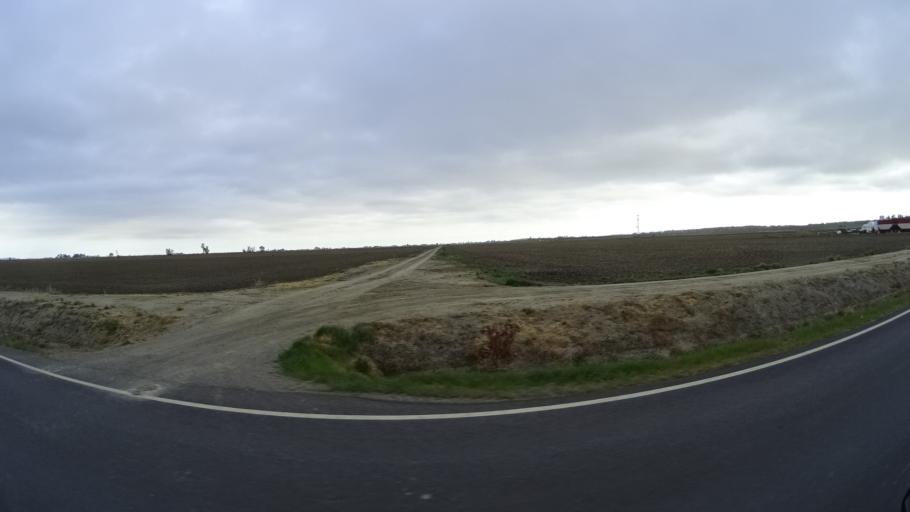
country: US
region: California
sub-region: Colusa County
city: Colusa
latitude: 39.4063
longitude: -122.0264
